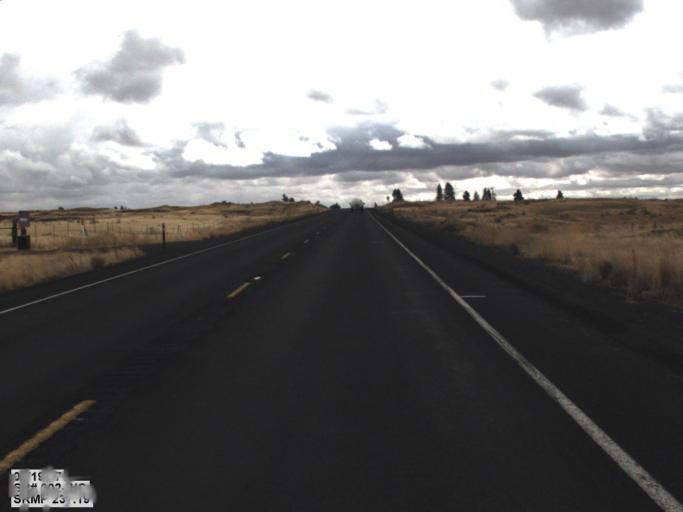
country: US
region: Washington
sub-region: Lincoln County
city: Davenport
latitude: 47.7027
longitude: -118.4113
